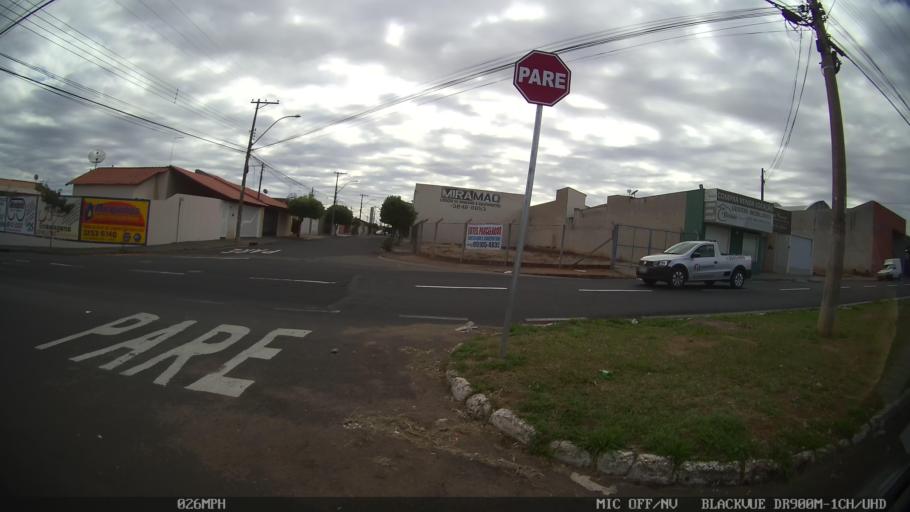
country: BR
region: Sao Paulo
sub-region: Sao Jose Do Rio Preto
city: Sao Jose do Rio Preto
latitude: -20.8034
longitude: -49.5004
